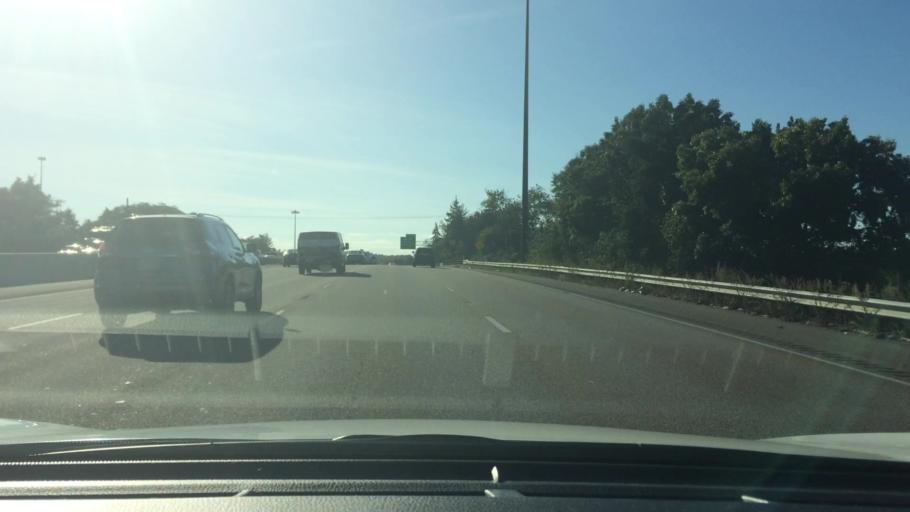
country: US
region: Massachusetts
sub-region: Middlesex County
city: Woburn
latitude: 42.4999
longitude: -71.1546
